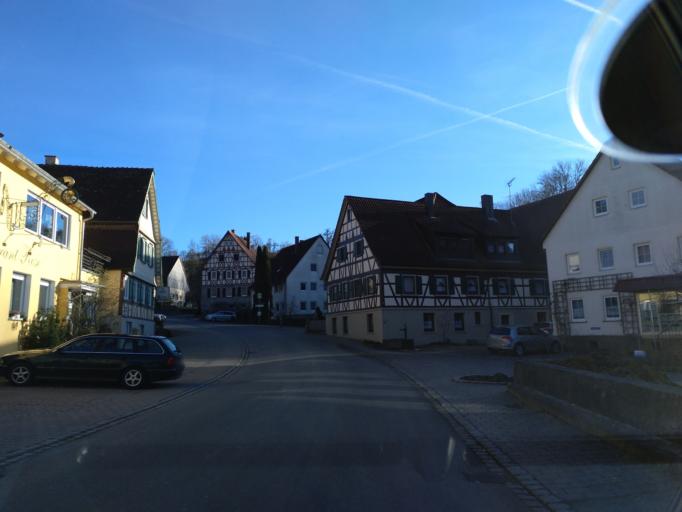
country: DE
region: Baden-Wuerttemberg
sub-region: Regierungsbezirk Stuttgart
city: Vellberg
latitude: 49.0832
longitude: 9.8950
